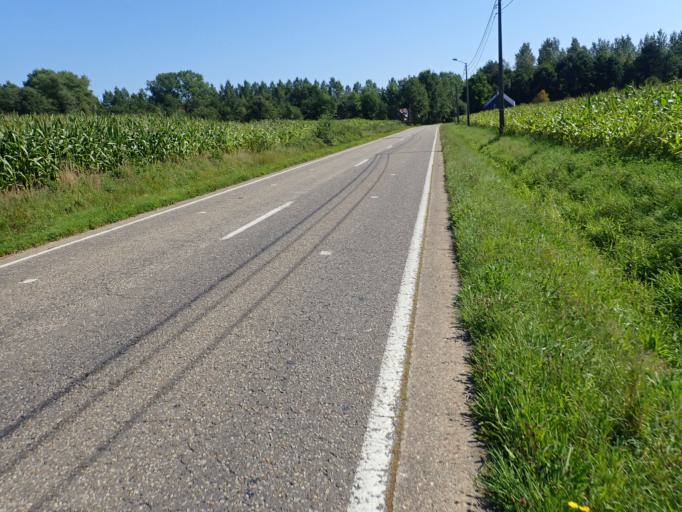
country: BE
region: Flanders
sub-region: Provincie Antwerpen
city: Herselt
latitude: 51.0541
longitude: 4.8469
